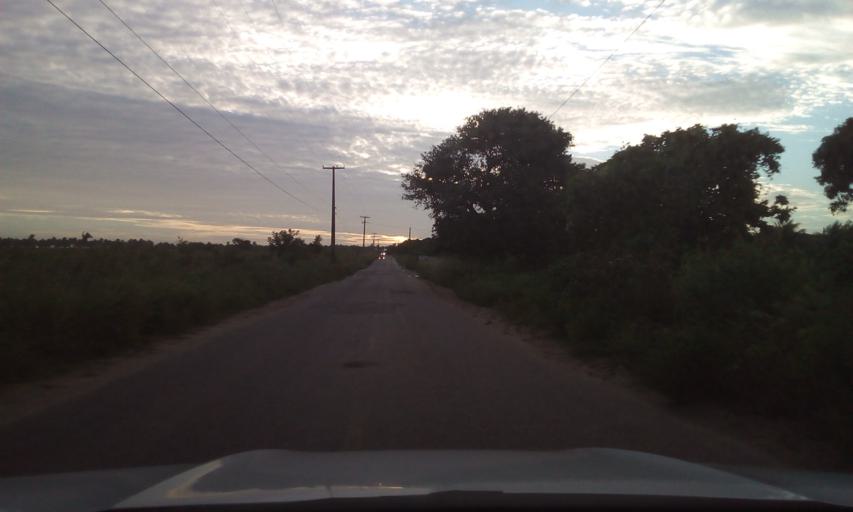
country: BR
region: Paraiba
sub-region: Conde
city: Conde
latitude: -7.2235
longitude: -34.8240
